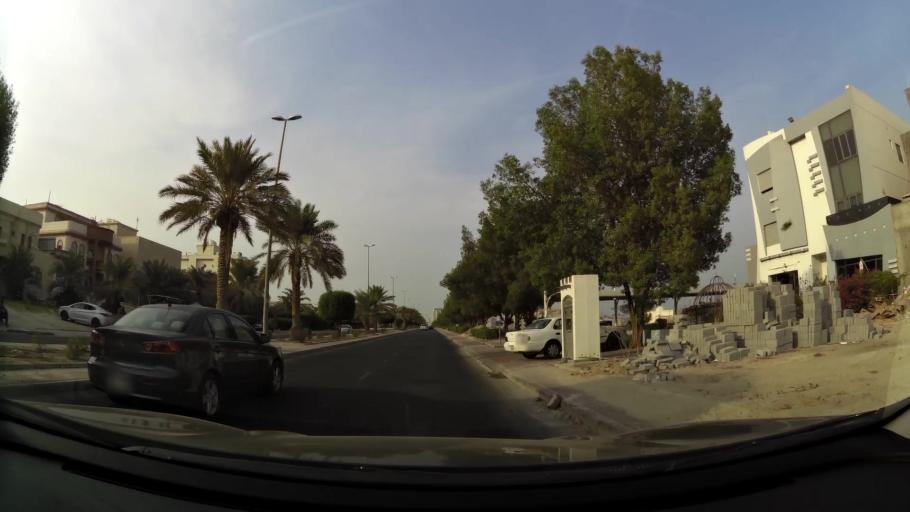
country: KW
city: Al Funaytis
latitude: 29.2336
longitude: 48.0845
